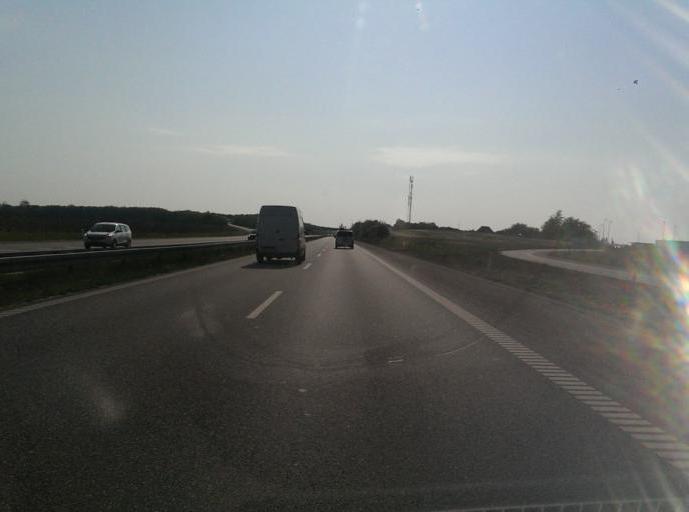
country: DK
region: South Denmark
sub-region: Esbjerg Kommune
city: Tjaereborg
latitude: 55.5205
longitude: 8.5556
